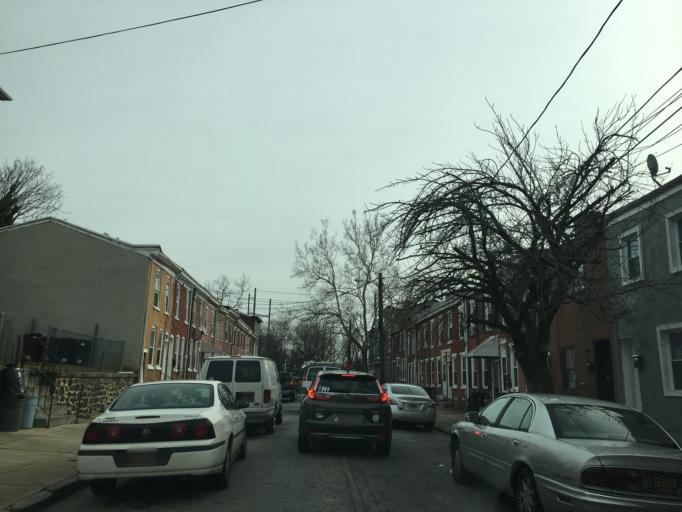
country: US
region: Delaware
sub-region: New Castle County
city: Wilmington
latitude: 39.7388
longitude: -75.5425
